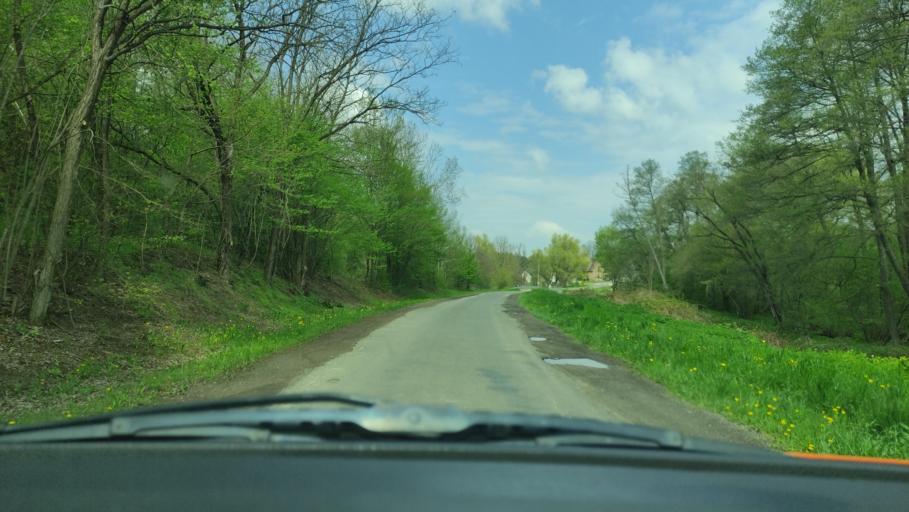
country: HU
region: Baranya
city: Sasd
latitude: 46.2845
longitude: 18.1029
